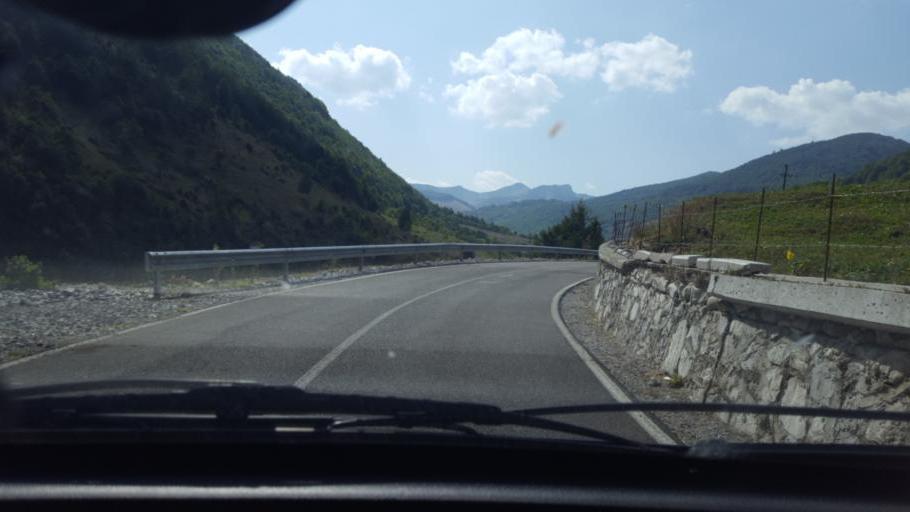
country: ME
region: Andrijevica
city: Andrijevica
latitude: 42.5582
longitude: 19.7307
